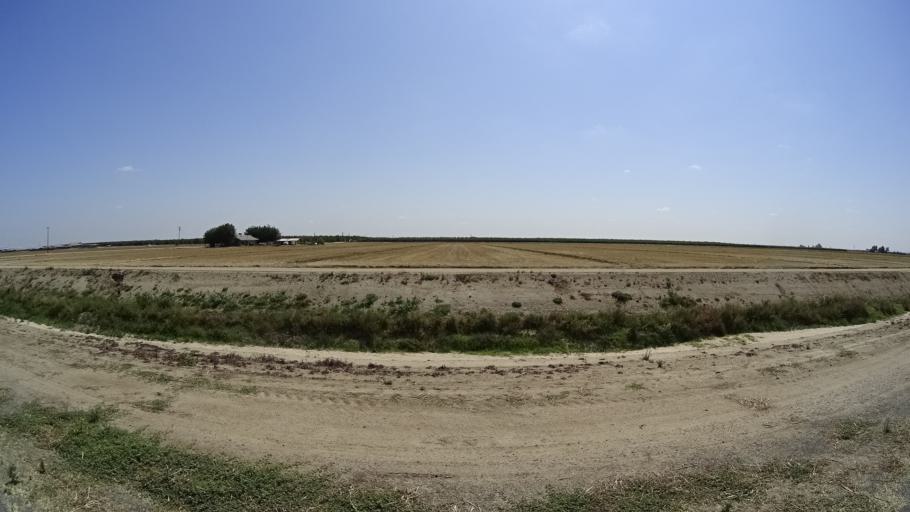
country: US
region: California
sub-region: Kings County
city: Home Garden
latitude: 36.2462
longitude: -119.6191
